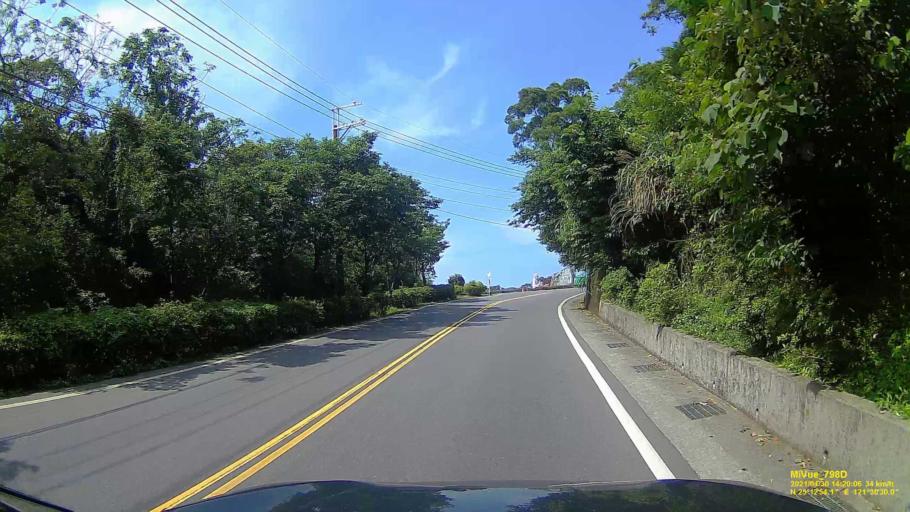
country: TW
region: Taipei
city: Taipei
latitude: 25.2152
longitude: 121.5084
